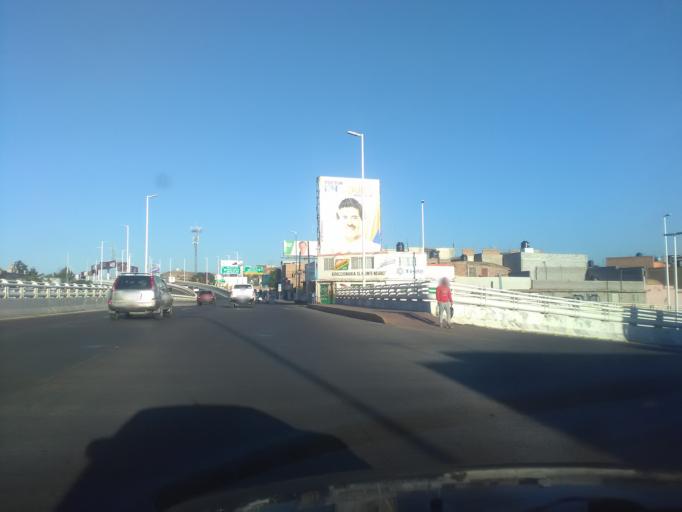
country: MX
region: Durango
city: Victoria de Durango
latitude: 24.0362
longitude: -104.6801
